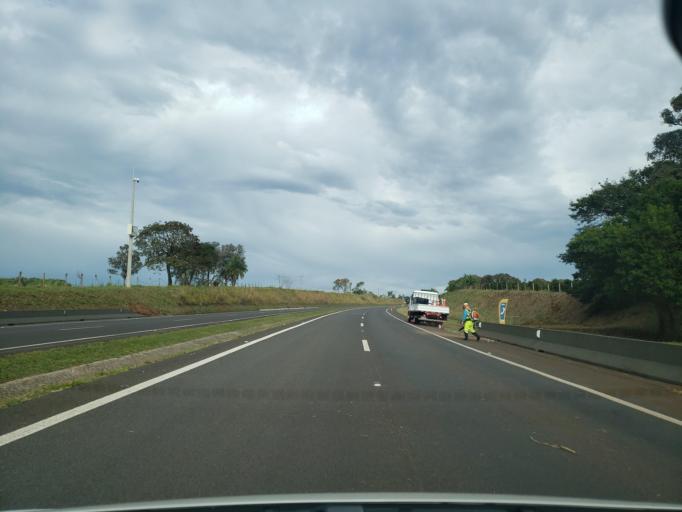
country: BR
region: Sao Paulo
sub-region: Dois Corregos
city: Dois Corregos
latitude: -22.2564
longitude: -48.3651
